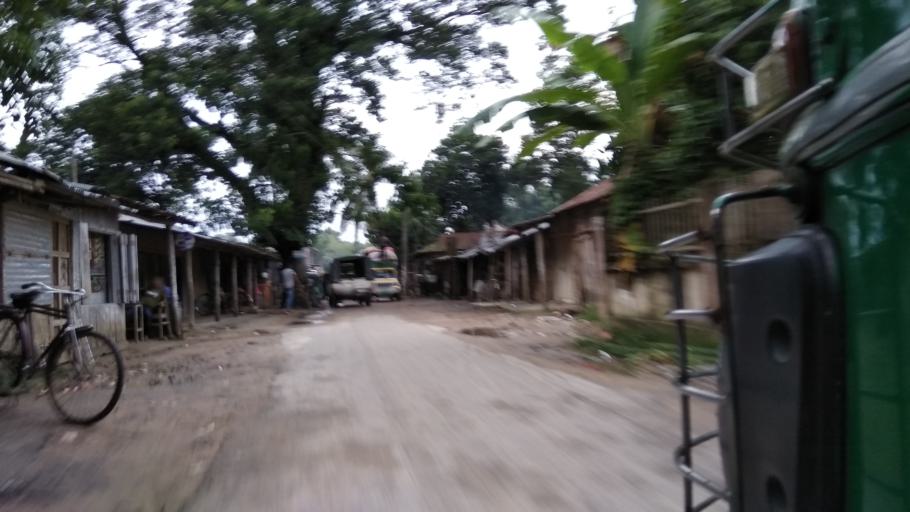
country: IN
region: Tripura
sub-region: Dhalai
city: Kamalpur
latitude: 24.2133
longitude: 91.8561
